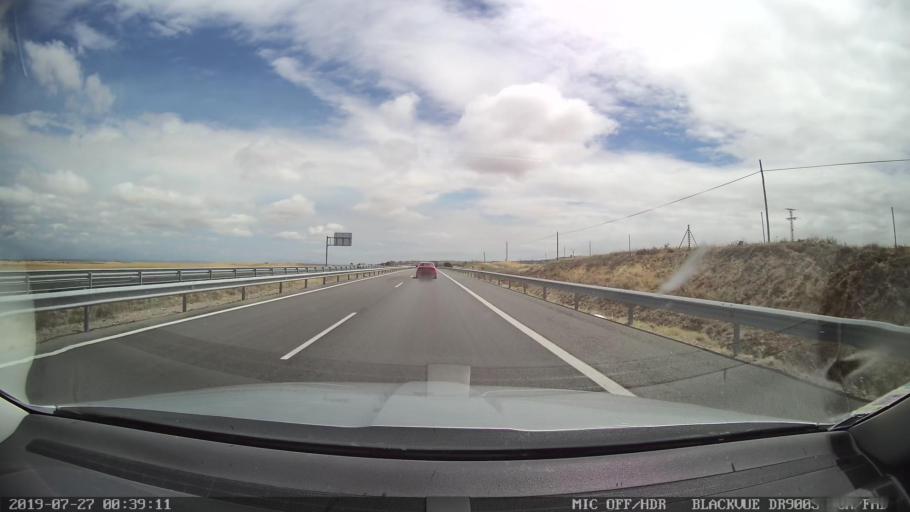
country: ES
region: Castille-La Mancha
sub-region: Province of Toledo
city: Herreruela de Oropesa
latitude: 39.9030
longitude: -5.2369
